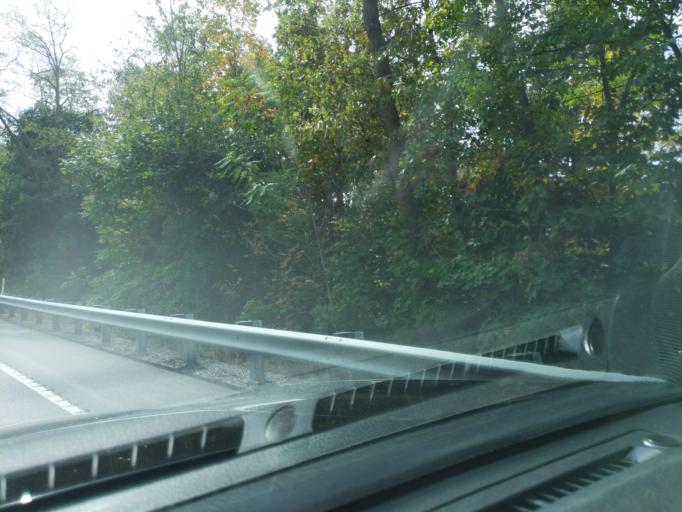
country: US
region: Pennsylvania
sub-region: Blair County
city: Lakemont
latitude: 40.4713
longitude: -78.3882
